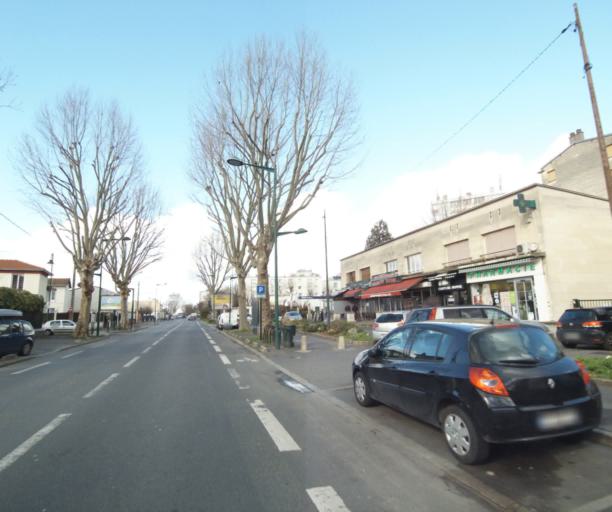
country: FR
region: Ile-de-France
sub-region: Departement de Seine-Saint-Denis
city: Villetaneuse
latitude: 48.9513
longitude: 2.3393
